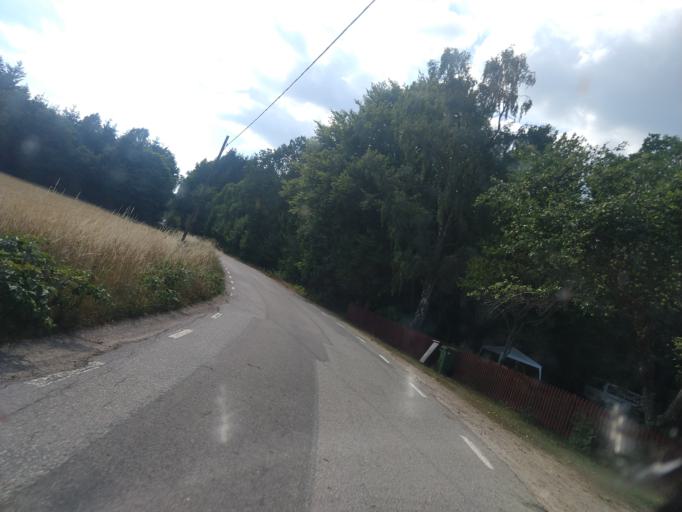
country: SE
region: Blekinge
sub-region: Karlskrona Kommun
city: Nattraby
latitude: 56.2574
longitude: 15.5215
